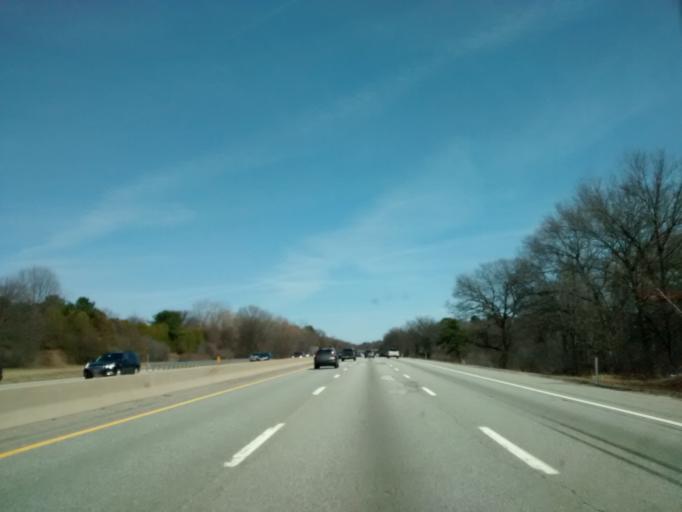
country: US
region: Massachusetts
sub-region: Middlesex County
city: Framingham Center
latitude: 42.3009
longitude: -71.4661
